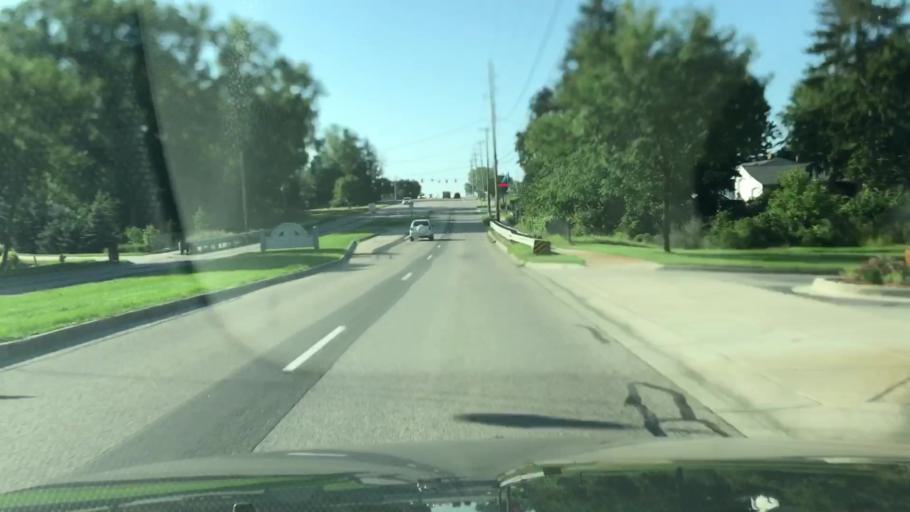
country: US
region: Michigan
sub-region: Kent County
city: Kentwood
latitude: 42.8574
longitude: -85.6251
